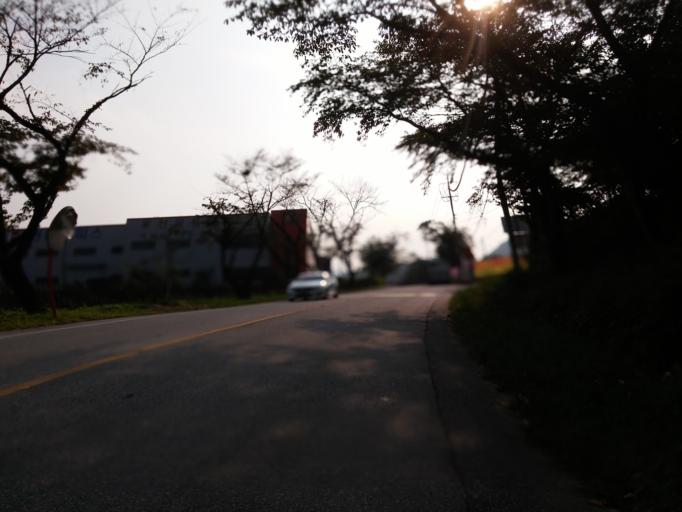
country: KR
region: Chungcheongbuk-do
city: Okcheon
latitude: 36.3192
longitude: 127.5811
